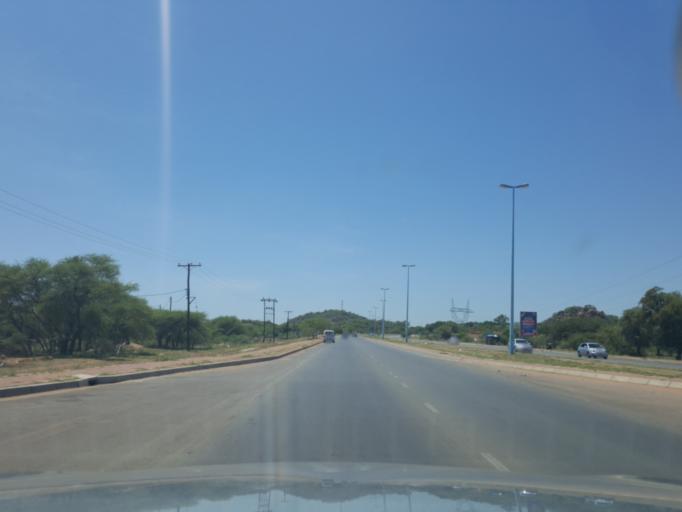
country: BW
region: Kweneng
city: Gaphatshwe
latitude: -24.5942
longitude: 25.8500
